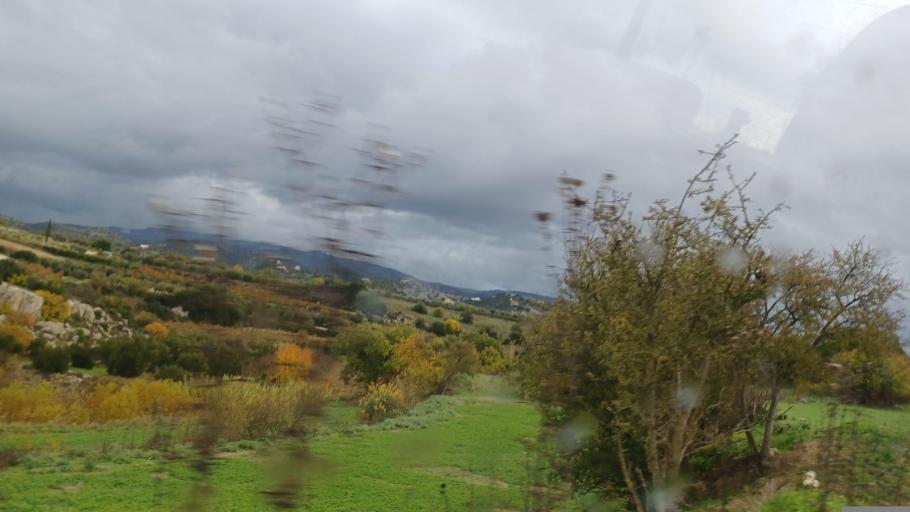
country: CY
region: Pafos
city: Mesogi
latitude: 34.8615
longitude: 32.5380
